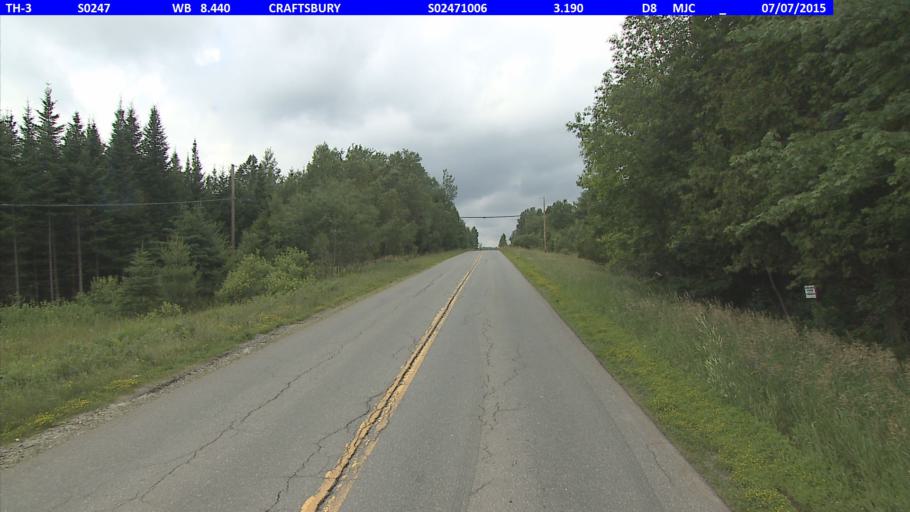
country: US
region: Vermont
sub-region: Caledonia County
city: Hardwick
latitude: 44.6526
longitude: -72.4085
